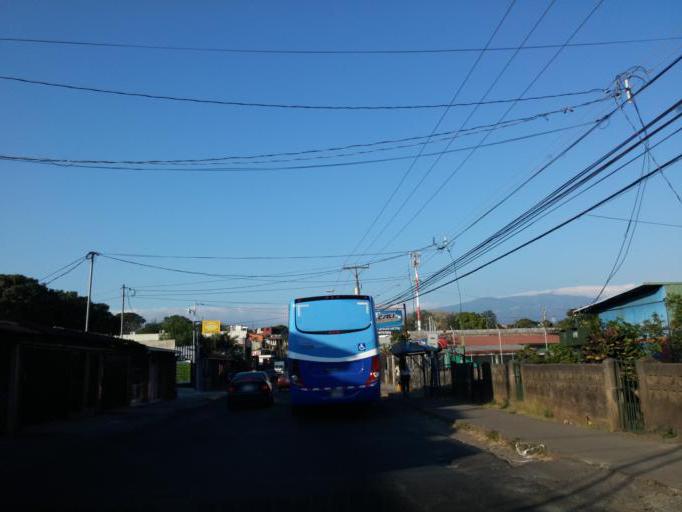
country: CR
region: Alajuela
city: Alajuela
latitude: 10.0021
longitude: -84.2194
